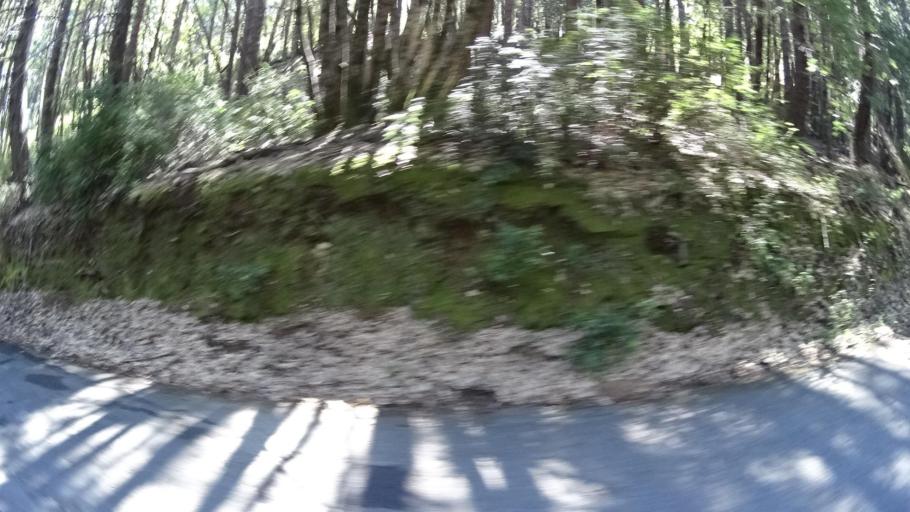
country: US
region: California
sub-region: Humboldt County
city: Redway
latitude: 40.1888
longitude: -124.0941
